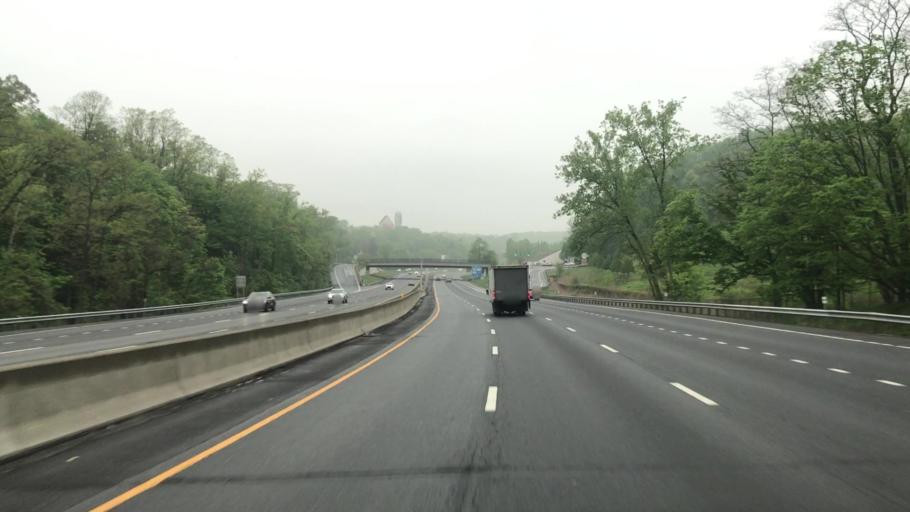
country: US
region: New York
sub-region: Westchester County
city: Tuckahoe
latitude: 40.9635
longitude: -73.8596
